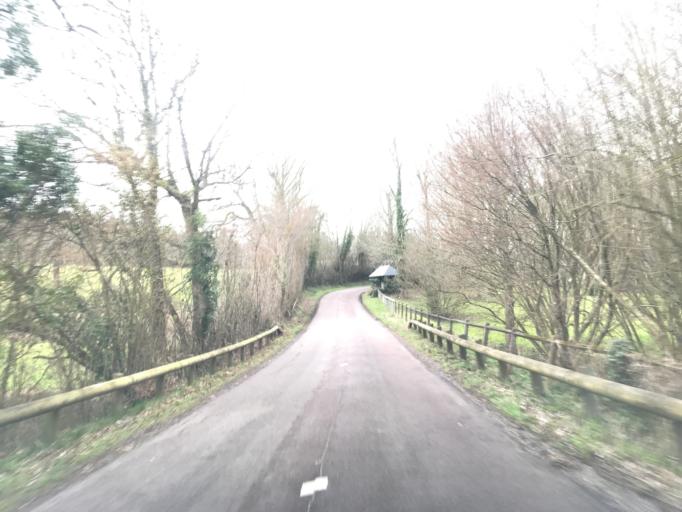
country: FR
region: Lower Normandy
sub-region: Departement du Calvados
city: Touques
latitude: 49.2782
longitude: 0.1044
